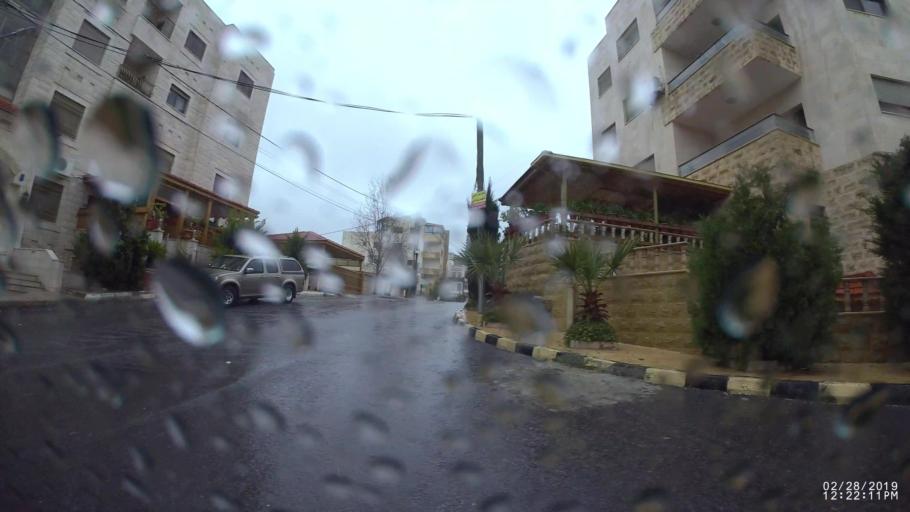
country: JO
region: Amman
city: Al Jubayhah
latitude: 32.0264
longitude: 35.8881
